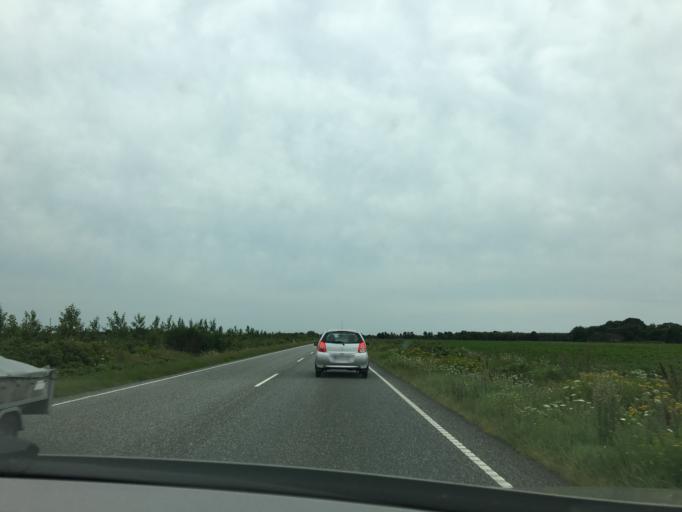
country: DK
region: Central Jutland
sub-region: Herning Kommune
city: Sunds
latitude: 56.2620
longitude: 9.0045
